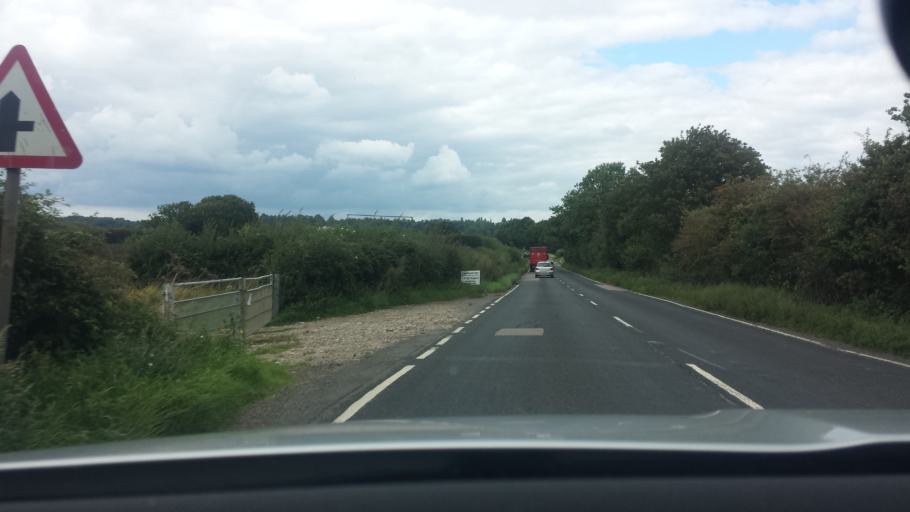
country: GB
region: England
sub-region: Kent
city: Marden
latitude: 51.2038
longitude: 0.5170
